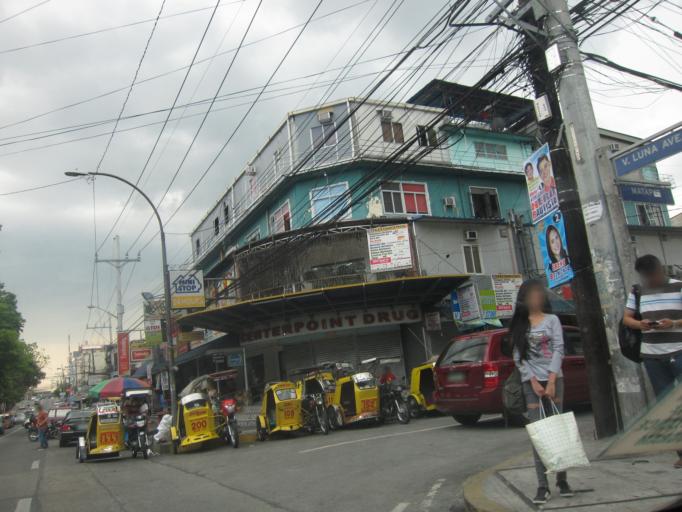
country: PH
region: Metro Manila
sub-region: Quezon City
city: Quezon City
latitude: 14.6366
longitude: 121.0527
